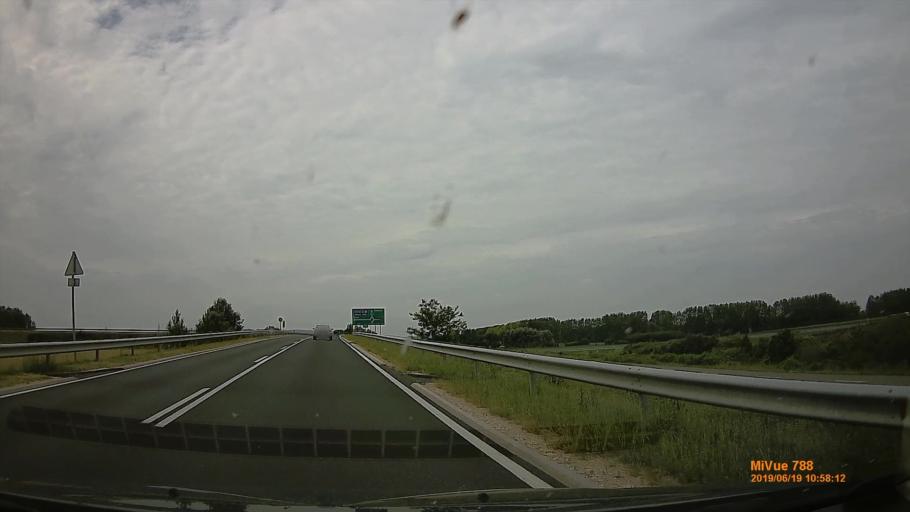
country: HU
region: Tolna
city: Tolna
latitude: 46.4165
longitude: 18.7364
